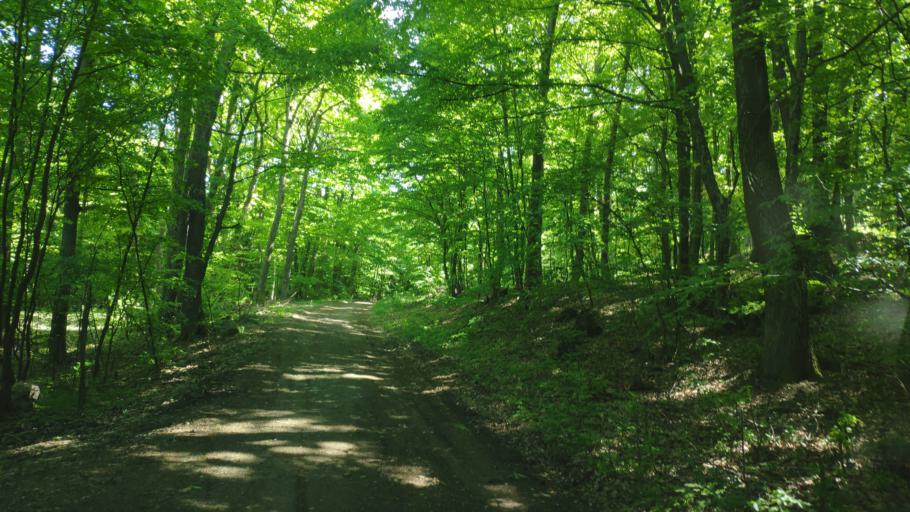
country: SK
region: Kosicky
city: Secovce
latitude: 48.7191
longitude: 21.5807
